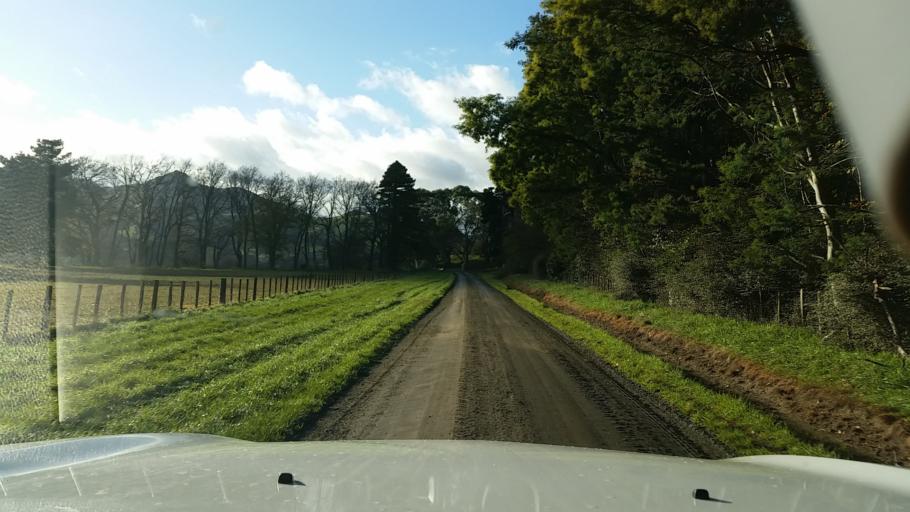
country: NZ
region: Wellington
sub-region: South Wairarapa District
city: Waipawa
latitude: -41.2647
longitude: 175.6792
